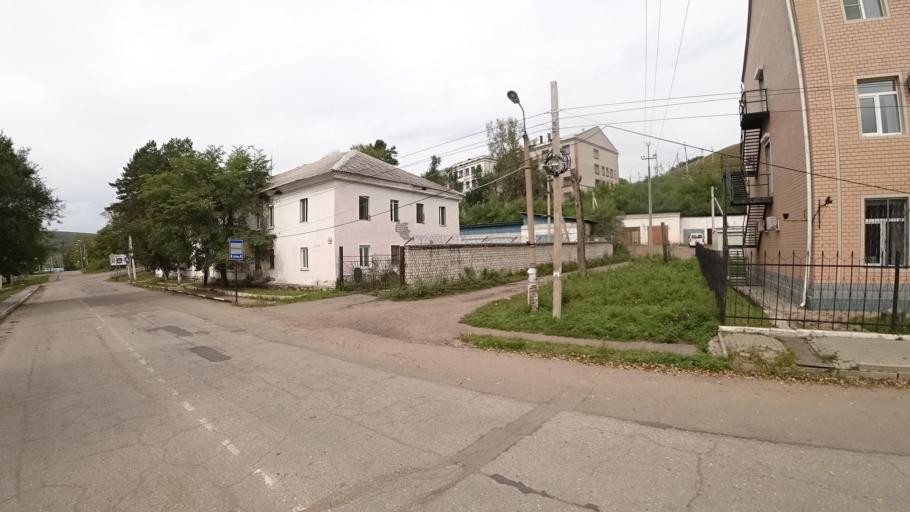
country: RU
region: Jewish Autonomous Oblast
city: Khingansk
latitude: 49.0201
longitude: 131.0611
